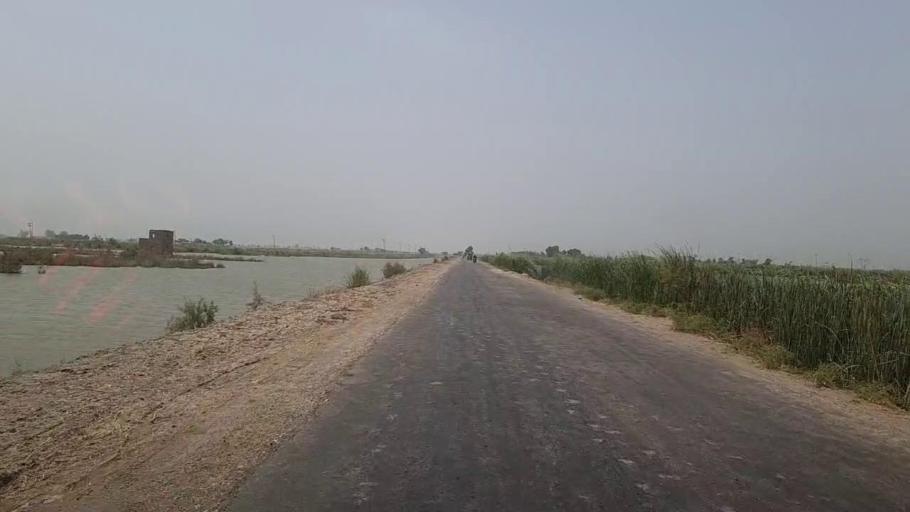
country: PK
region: Sindh
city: Radhan
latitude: 27.1511
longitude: 67.9386
